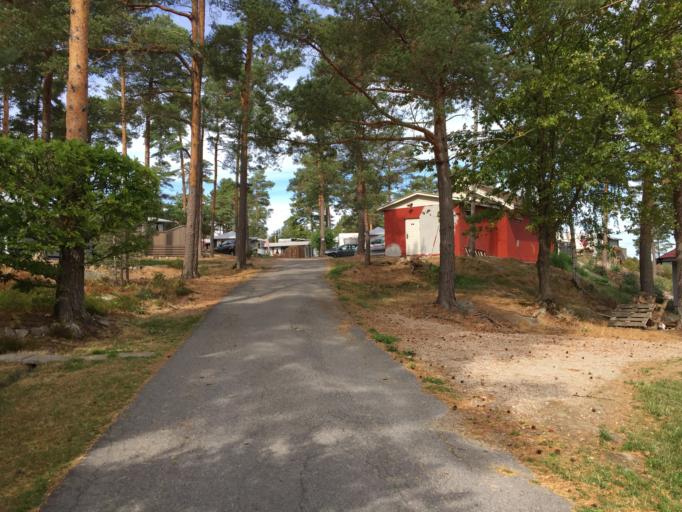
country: NO
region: Ostfold
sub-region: Fredrikstad
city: Fredrikstad
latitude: 59.1021
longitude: 10.9330
